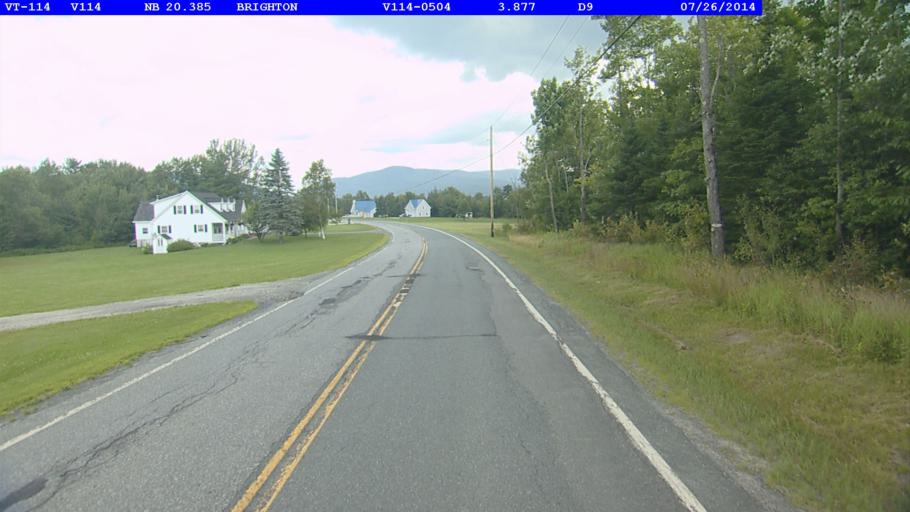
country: US
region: Vermont
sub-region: Caledonia County
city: Lyndonville
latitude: 44.7893
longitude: -71.9095
